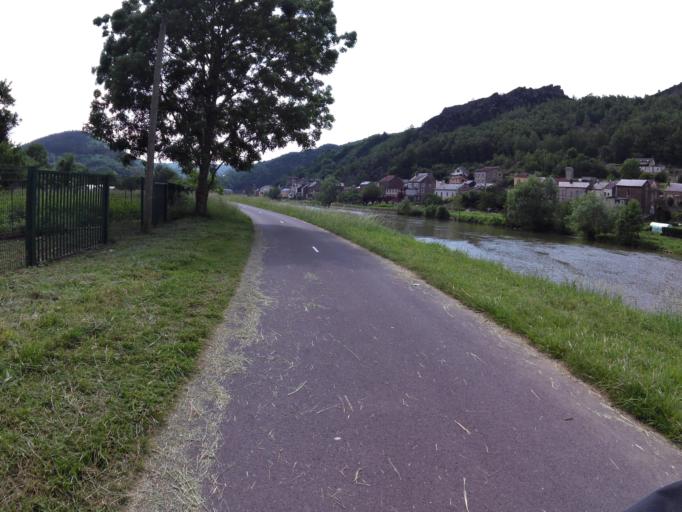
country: FR
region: Champagne-Ardenne
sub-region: Departement des Ardennes
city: Montherme
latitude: 49.8609
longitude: 4.7486
